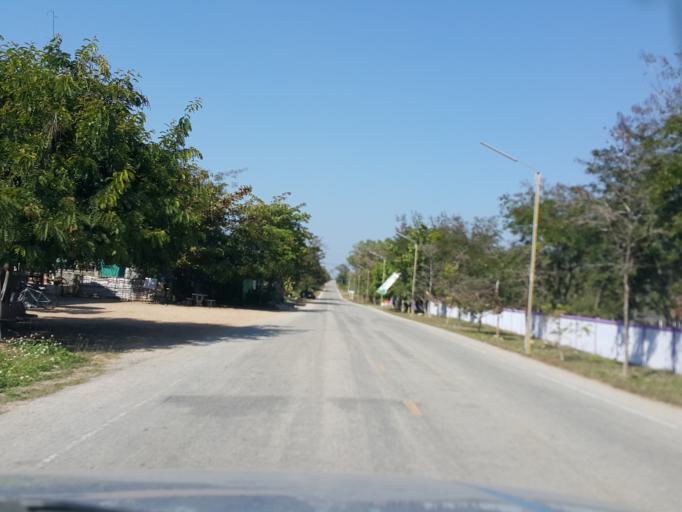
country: TH
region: Chiang Mai
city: Doi Lo
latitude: 18.5389
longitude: 98.7969
